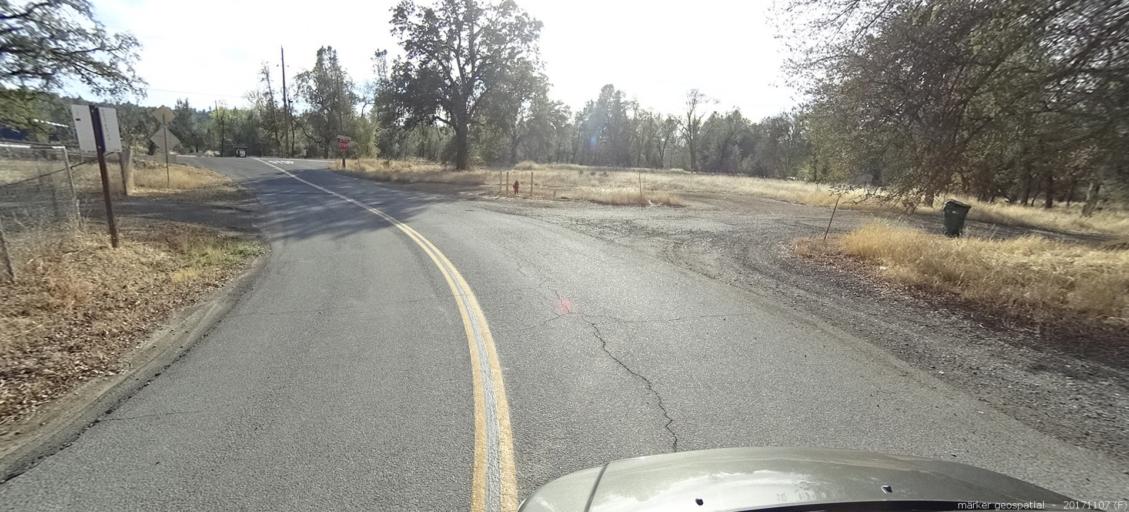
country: US
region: California
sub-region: Shasta County
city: Redding
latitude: 40.5021
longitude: -122.4518
